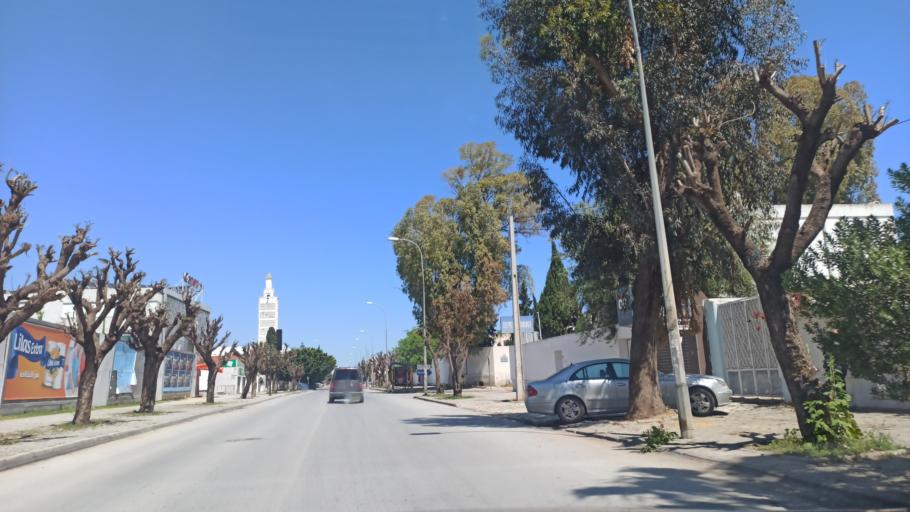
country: TN
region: Tunis
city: Tunis
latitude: 36.8256
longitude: 10.1824
